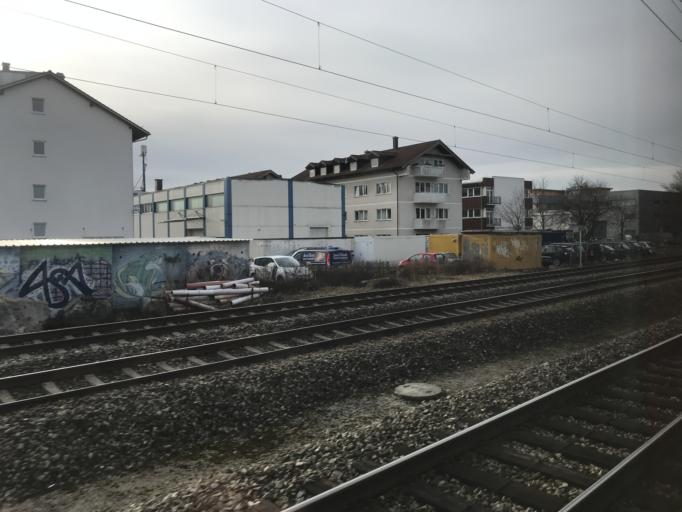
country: DE
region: Bavaria
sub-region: Upper Bavaria
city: Grobenzell
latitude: 48.1864
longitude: 11.3898
